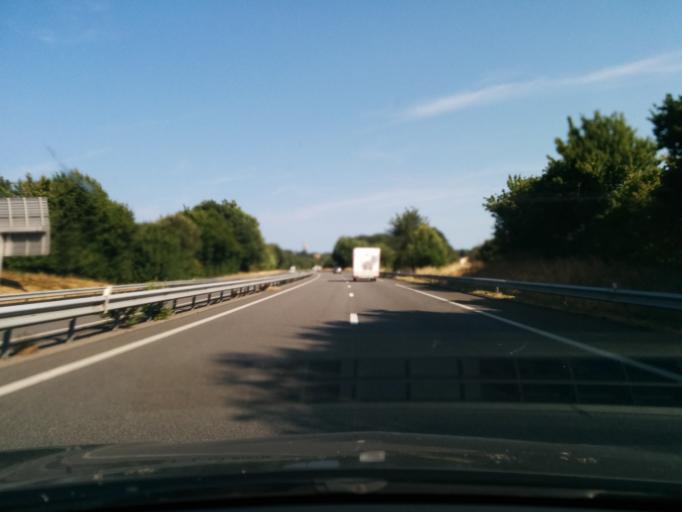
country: FR
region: Limousin
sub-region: Departement de la Haute-Vienne
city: Saint-Germain-les-Belles
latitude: 45.5766
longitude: 1.4848
